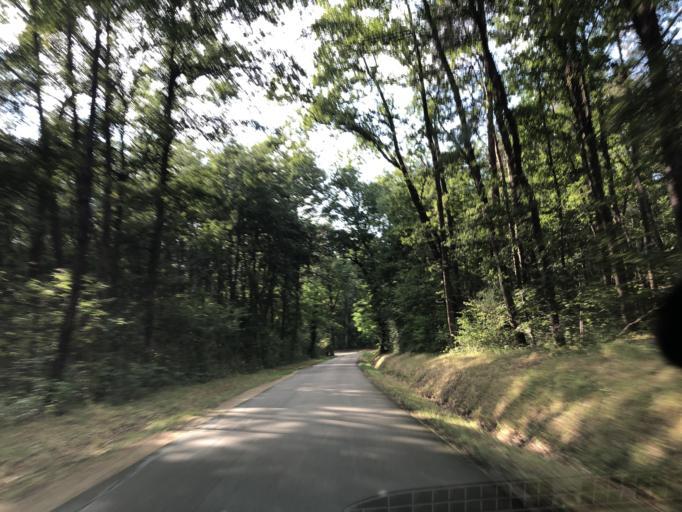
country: FR
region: Bourgogne
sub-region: Departement de l'Yonne
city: Charbuy
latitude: 47.8202
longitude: 3.5002
